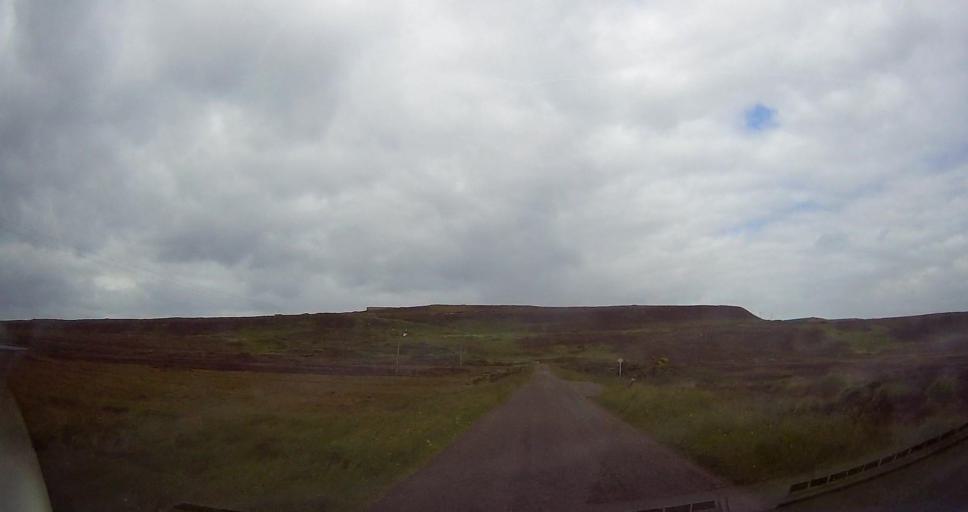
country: GB
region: Scotland
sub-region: Highland
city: Thurso
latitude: 58.6553
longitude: -3.3704
